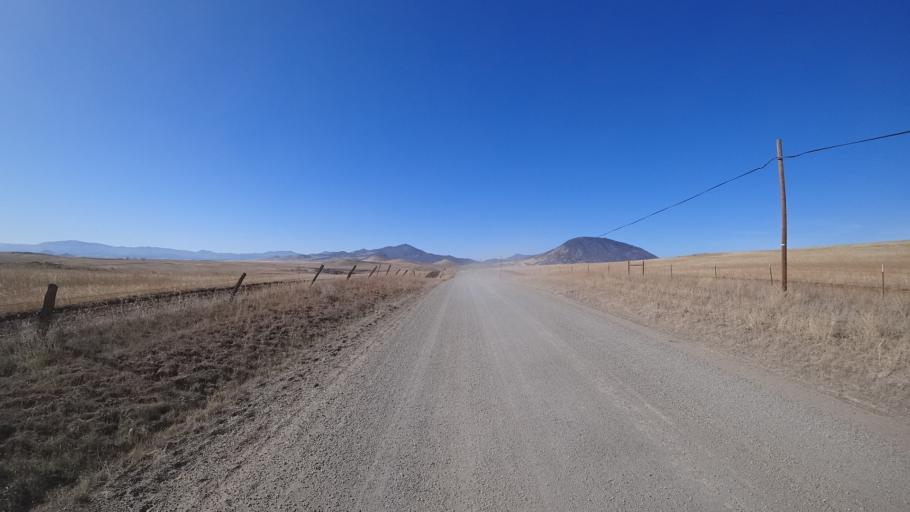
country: US
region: California
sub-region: Siskiyou County
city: Montague
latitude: 41.8298
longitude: -122.4134
